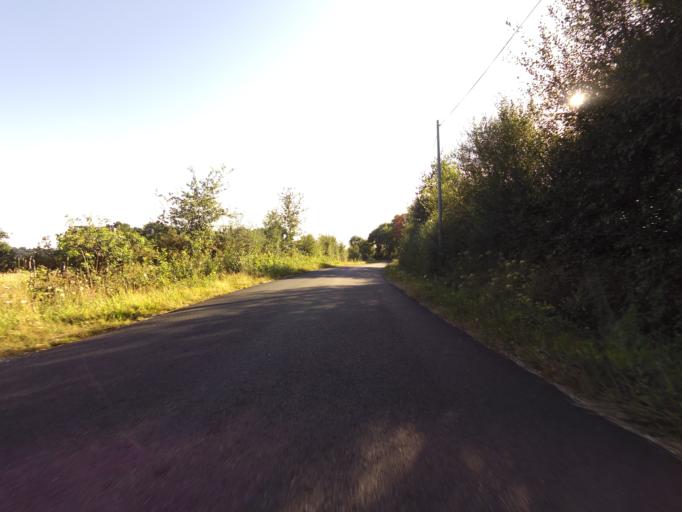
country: FR
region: Brittany
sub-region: Departement du Morbihan
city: Pluherlin
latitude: 47.7212
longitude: -2.3525
